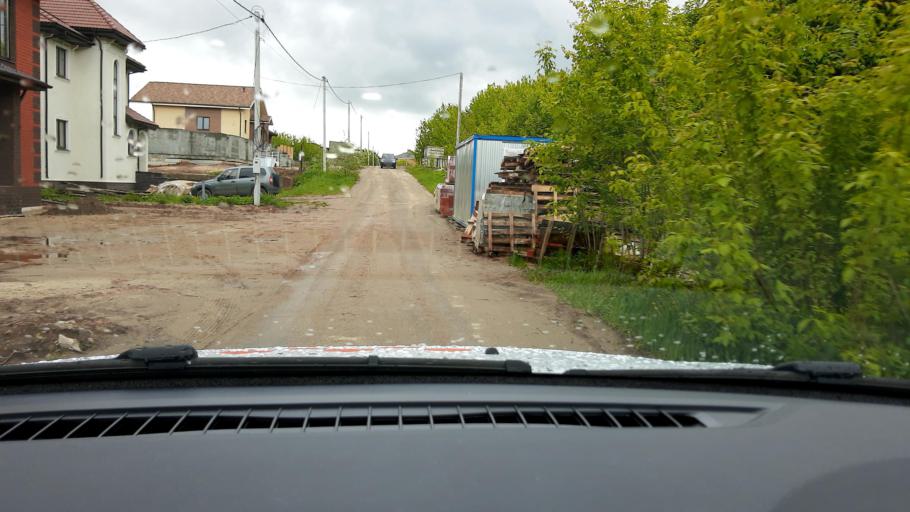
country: RU
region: Nizjnij Novgorod
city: Afonino
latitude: 56.2710
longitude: 44.0987
